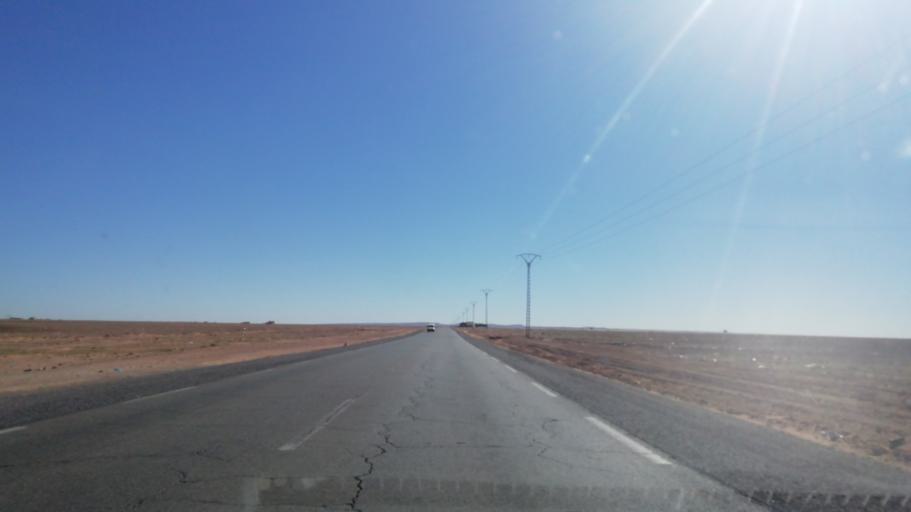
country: DZ
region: Saida
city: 'Ain el Hadjar
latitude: 34.0163
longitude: 0.1101
